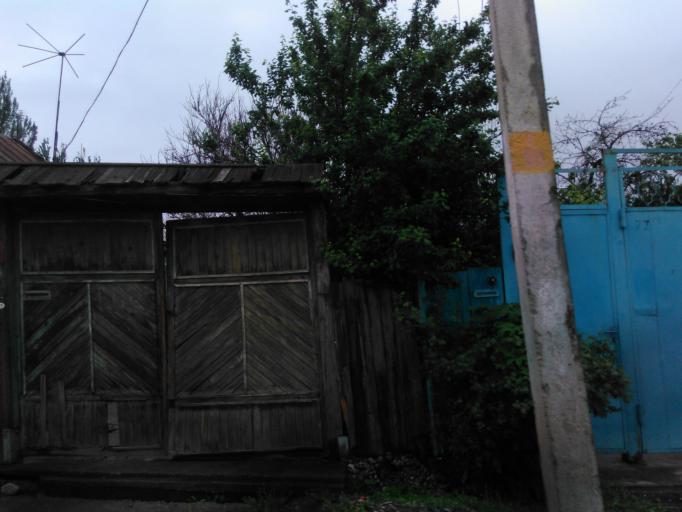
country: KG
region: Chuy
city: Tokmok
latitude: 42.8168
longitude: 75.3182
